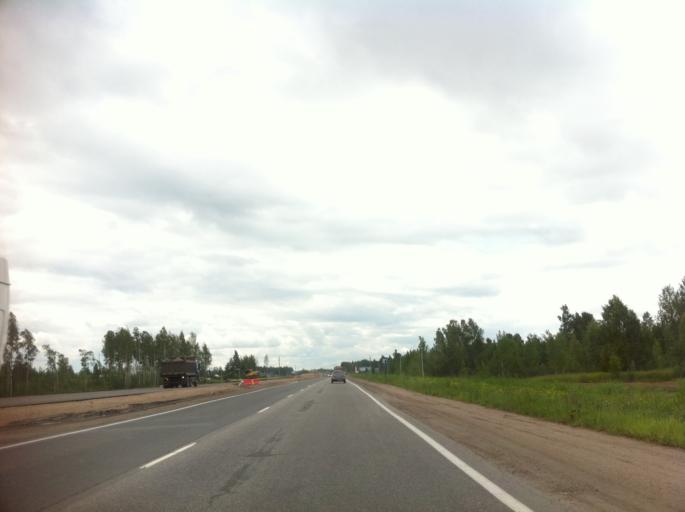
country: RU
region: Leningrad
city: Gatchina
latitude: 59.5683
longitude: 30.1681
